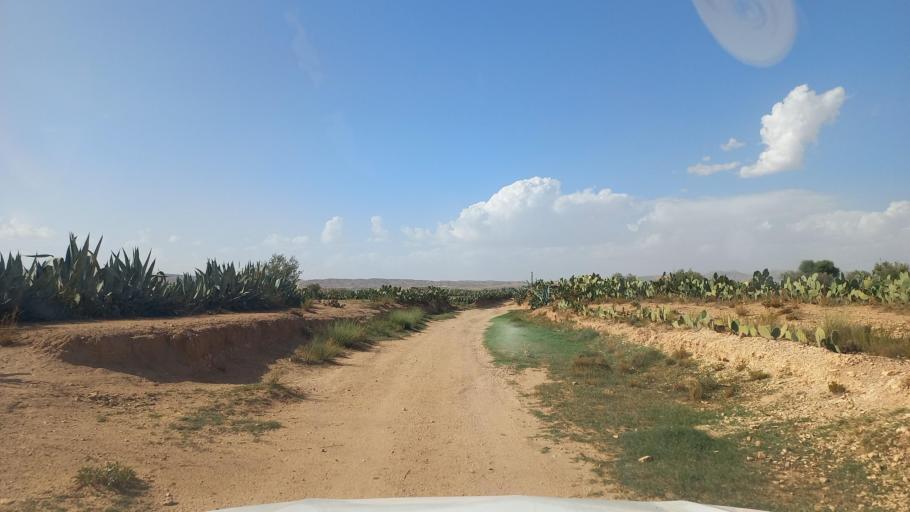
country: TN
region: Al Qasrayn
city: Sbiba
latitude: 35.3127
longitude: 9.0315
